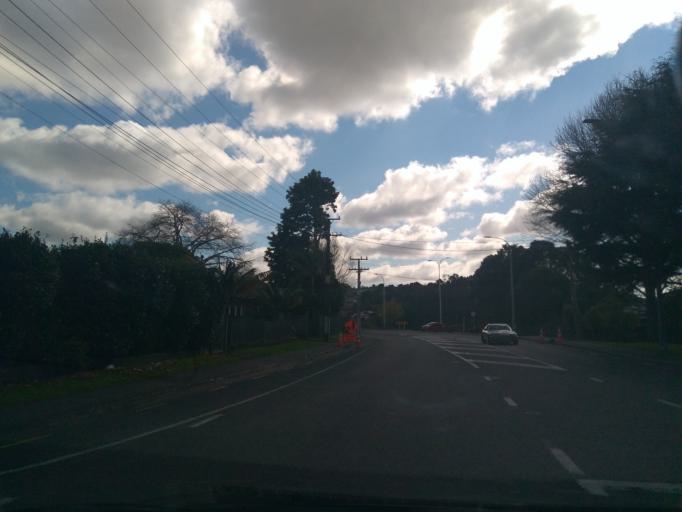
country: NZ
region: Northland
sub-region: Whangarei
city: Whangarei
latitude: -35.7039
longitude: 174.3266
